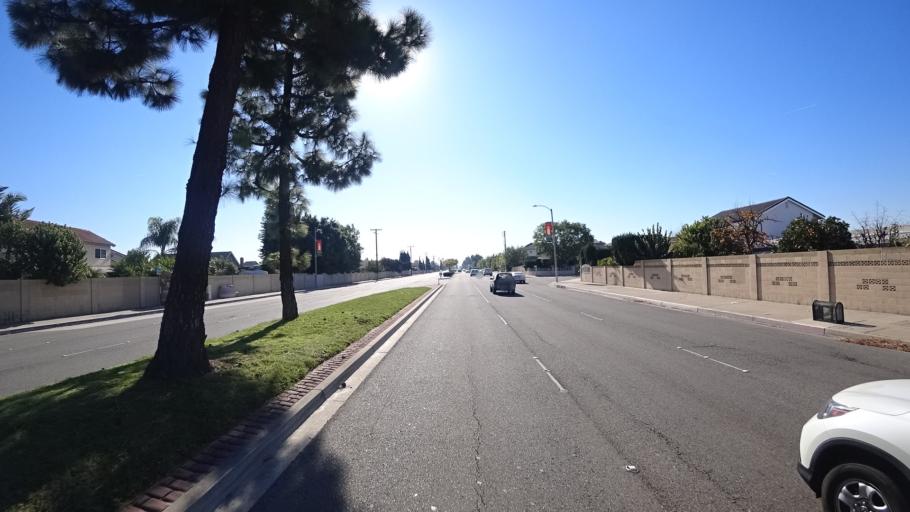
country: US
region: California
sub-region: Orange County
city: Garden Grove
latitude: 33.7496
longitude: -117.9551
